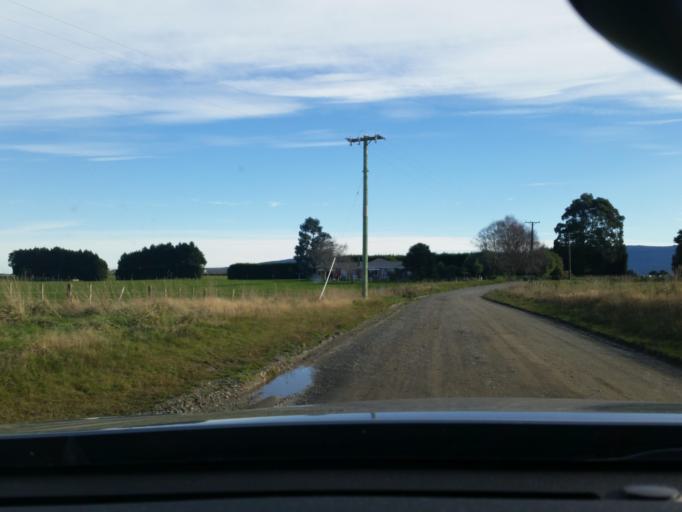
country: NZ
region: Southland
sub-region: Southland District
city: Riverton
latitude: -46.2713
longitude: 168.0307
